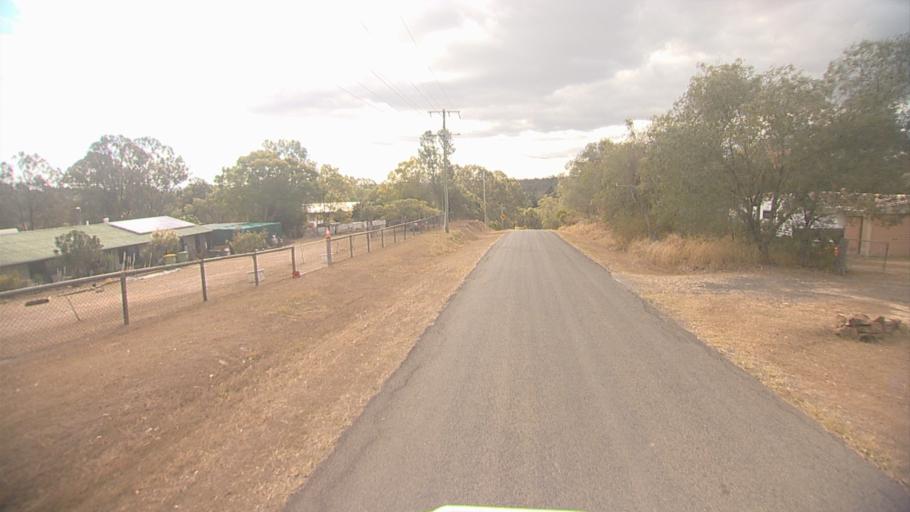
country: AU
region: Queensland
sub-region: Logan
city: Cedar Vale
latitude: -27.8885
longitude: 153.0235
